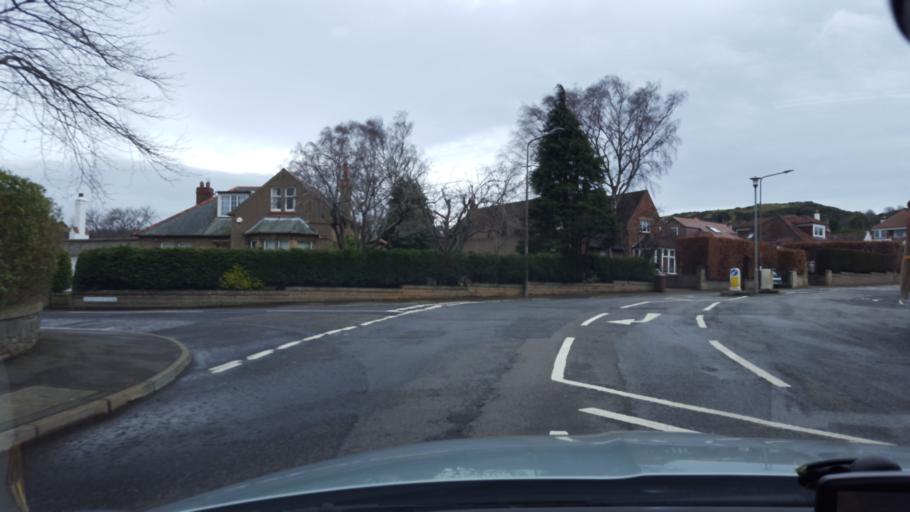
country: GB
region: Scotland
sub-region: Edinburgh
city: Edinburgh
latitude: 55.9172
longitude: -3.2118
